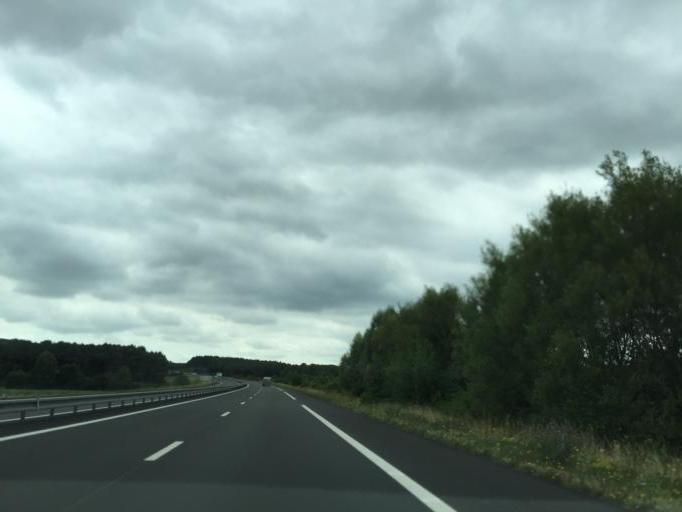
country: FR
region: Pays de la Loire
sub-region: Departement de la Sarthe
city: Teloche
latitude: 47.8636
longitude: 0.2995
